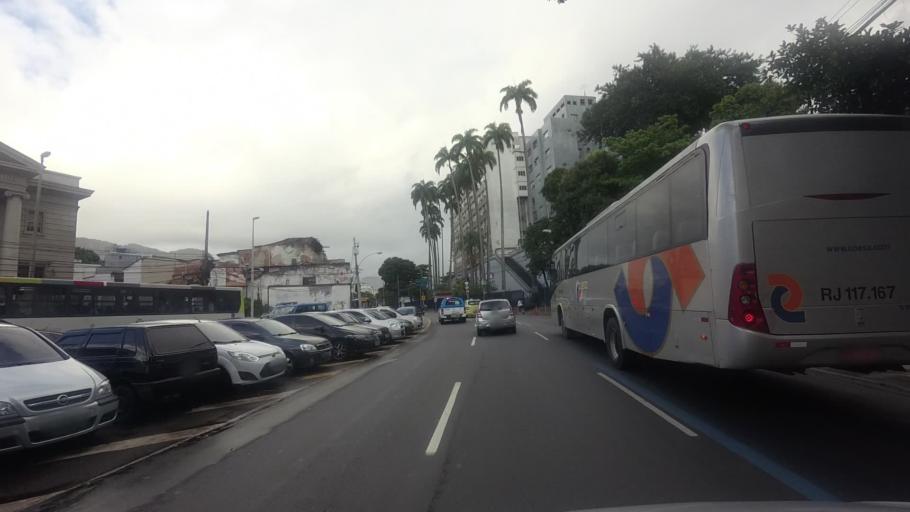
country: BR
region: Rio de Janeiro
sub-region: Rio De Janeiro
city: Rio de Janeiro
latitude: -22.9130
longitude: -43.2027
